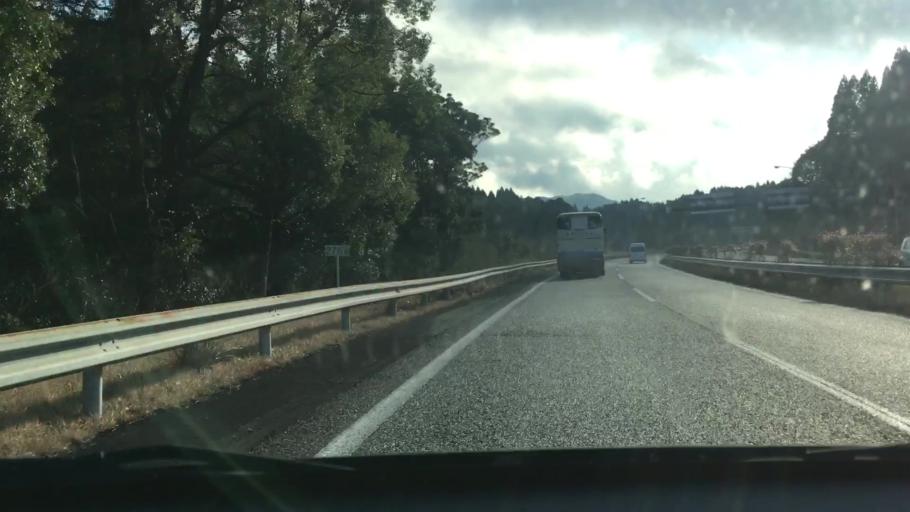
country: JP
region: Kagoshima
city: Okuchi-shinohara
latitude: 32.0301
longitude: 130.7975
